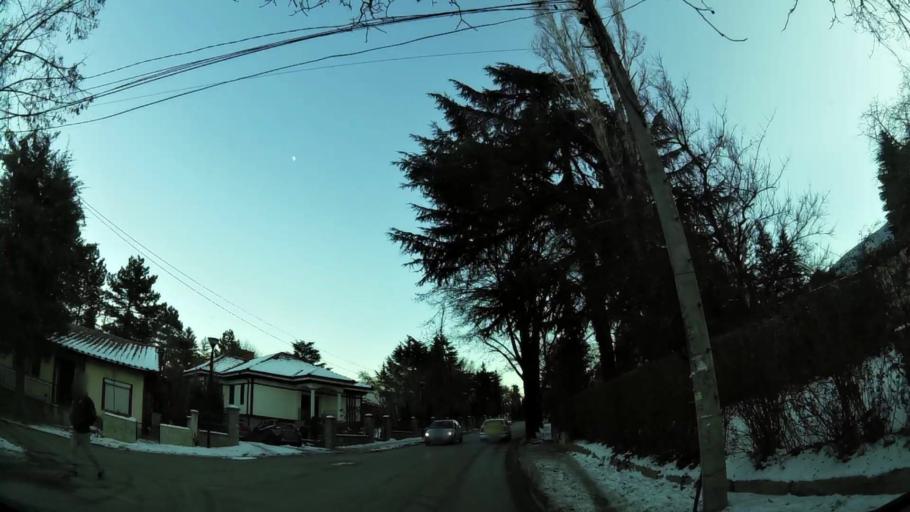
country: MK
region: Karpos
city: Skopje
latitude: 41.9895
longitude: 21.4121
